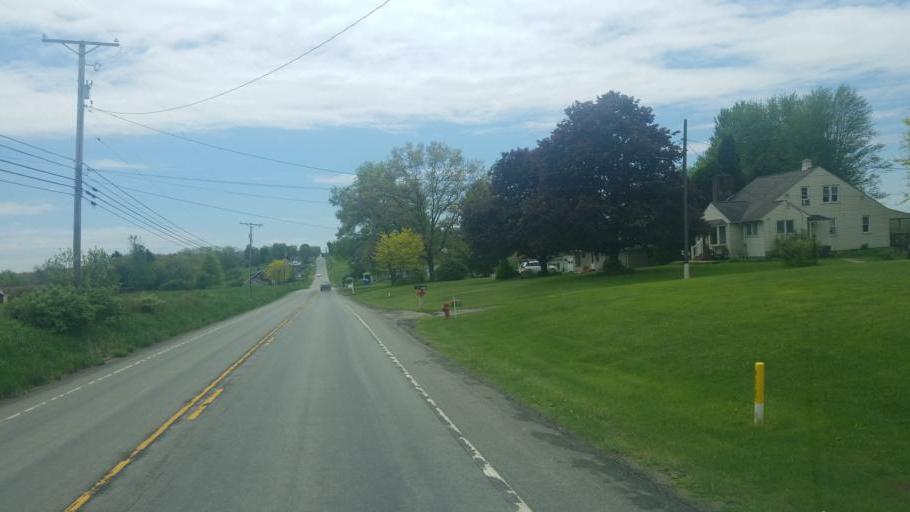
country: US
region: Pennsylvania
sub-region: Clarion County
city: Marianne
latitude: 41.2621
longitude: -79.4592
